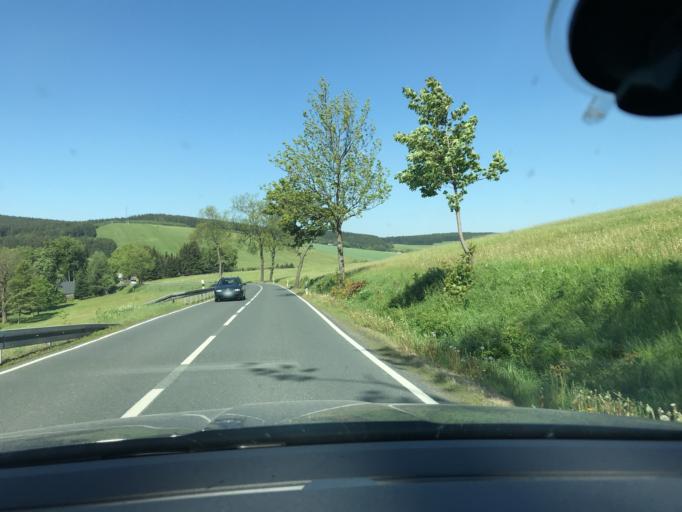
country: DE
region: Saxony
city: Kurort Oberwiesenthal
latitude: 50.4670
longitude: 12.9782
